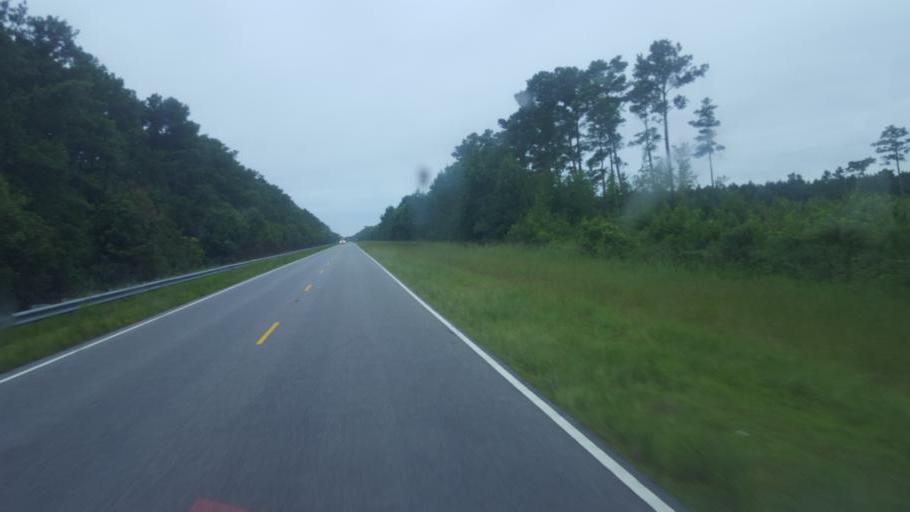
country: US
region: North Carolina
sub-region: Tyrrell County
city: Columbia
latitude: 35.9179
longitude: -76.1244
